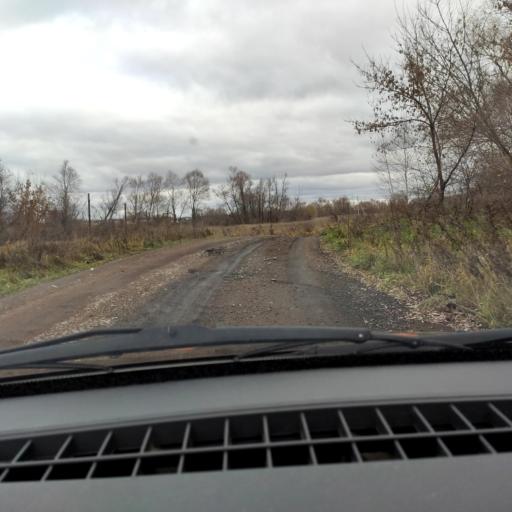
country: RU
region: Bashkortostan
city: Avdon
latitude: 54.4908
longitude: 55.8525
